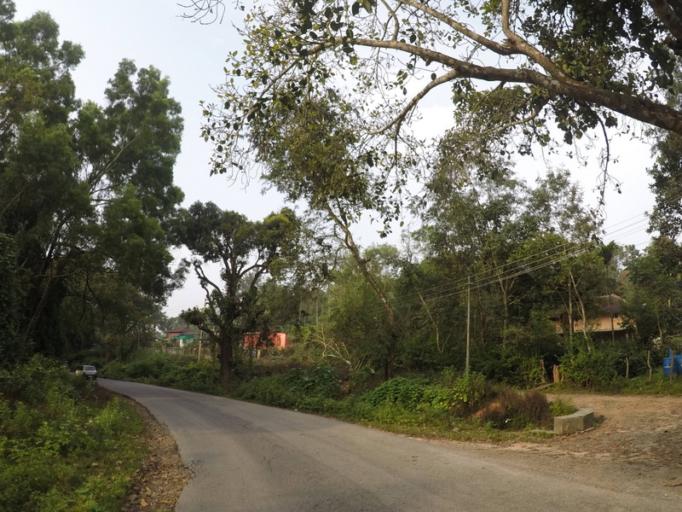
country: IN
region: Karnataka
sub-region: Chikmagalur
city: Chikmagalur
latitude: 13.2652
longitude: 75.6870
